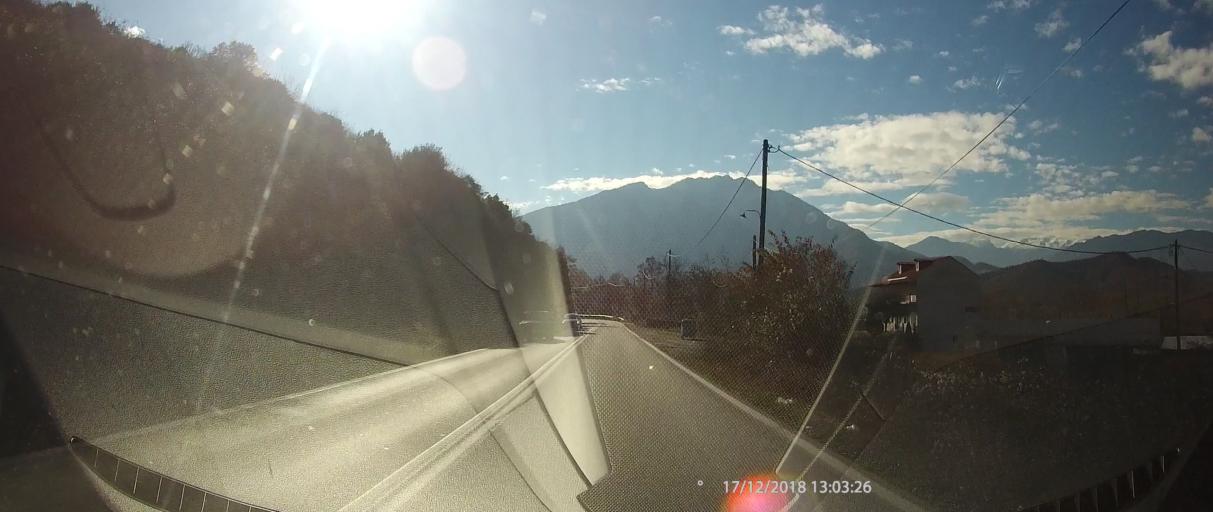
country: GR
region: Thessaly
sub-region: Trikala
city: Kastraki
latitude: 39.7126
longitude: 21.6019
